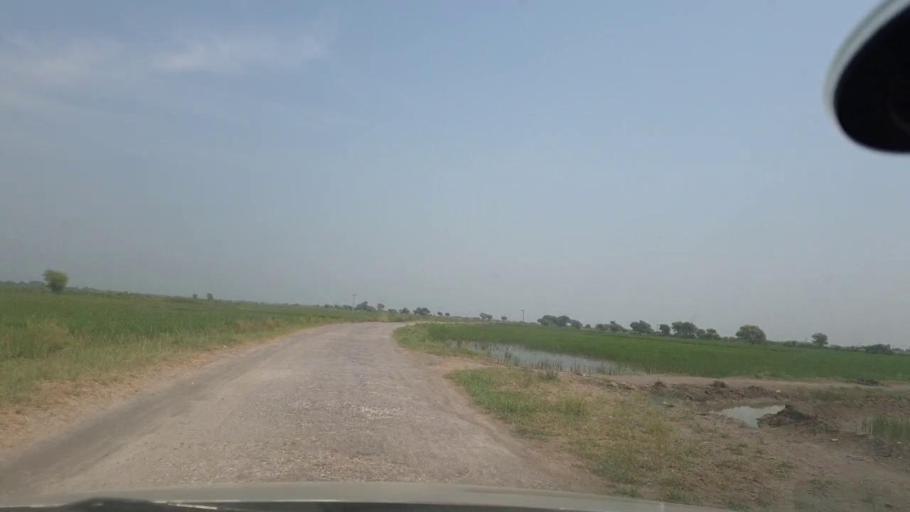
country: PK
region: Sindh
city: Jacobabad
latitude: 28.1392
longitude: 68.3678
